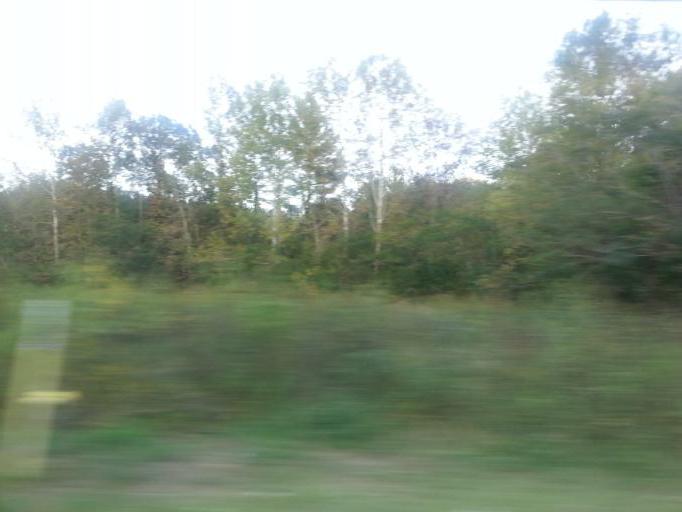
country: US
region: Tennessee
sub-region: Anderson County
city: Rocky Top
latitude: 36.2418
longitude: -84.1651
